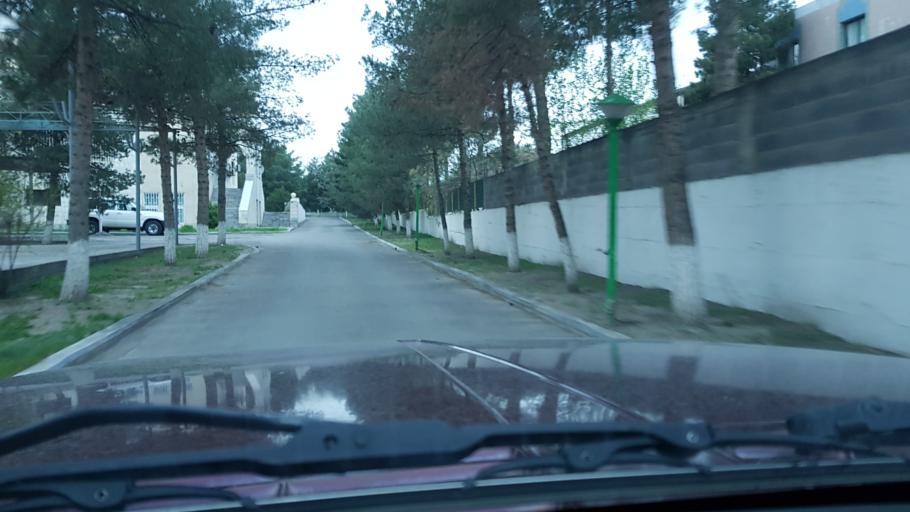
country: TM
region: Ahal
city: Ashgabat
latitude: 37.8848
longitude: 58.3625
